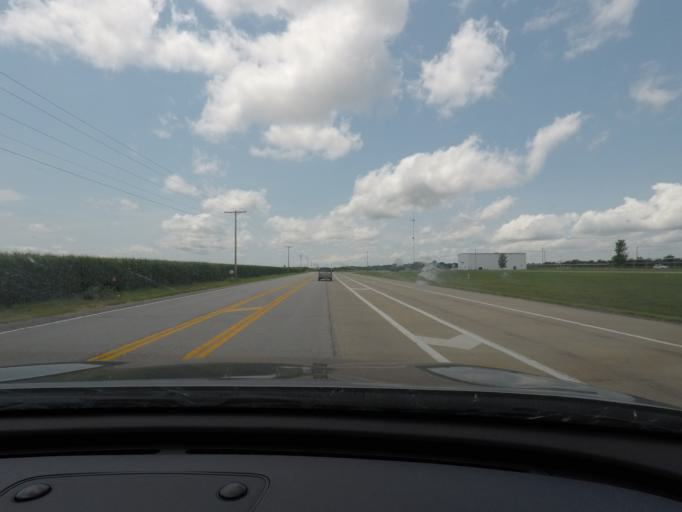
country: US
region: Missouri
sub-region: Saline County
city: Marshall
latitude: 39.1945
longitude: -93.3819
